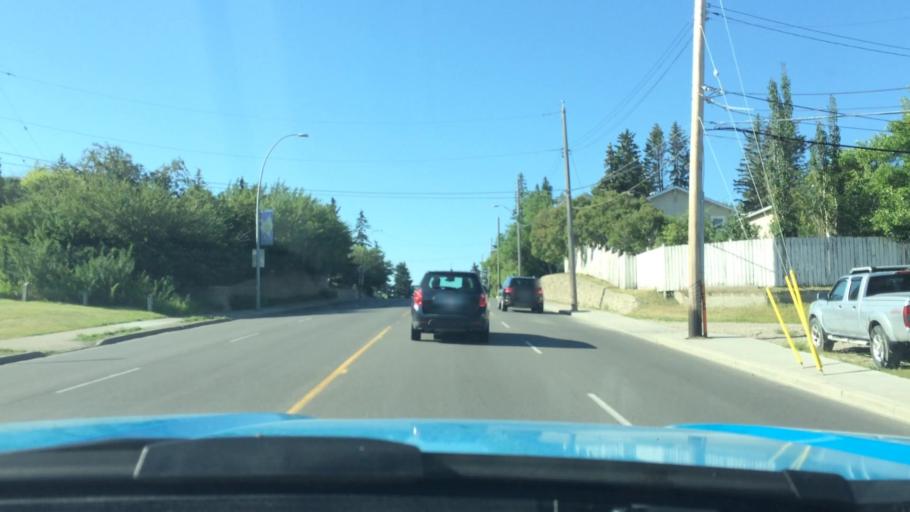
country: CA
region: Alberta
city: Calgary
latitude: 51.0740
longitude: -114.0948
